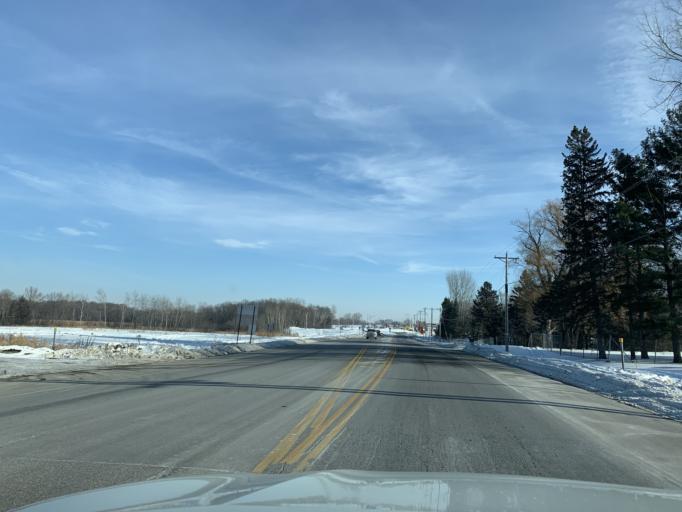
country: US
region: Minnesota
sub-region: Anoka County
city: Columbus
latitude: 45.2504
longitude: -93.0337
